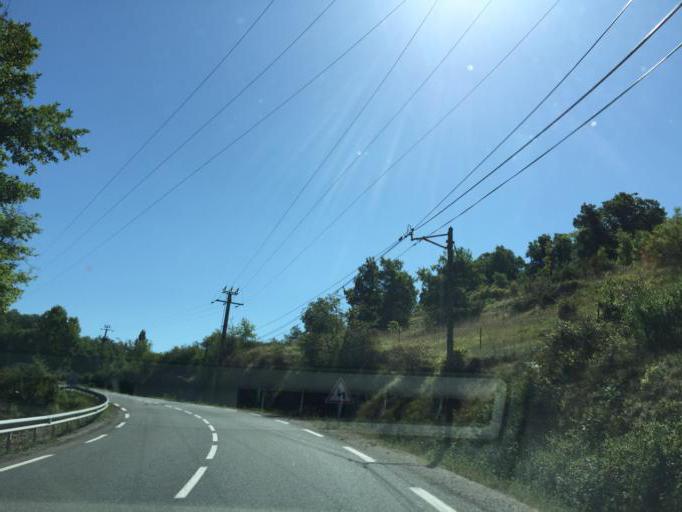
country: FR
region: Midi-Pyrenees
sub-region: Departement de l'Aveyron
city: Saint-Georges-de-Luzencon
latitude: 44.0105
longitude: 2.9747
